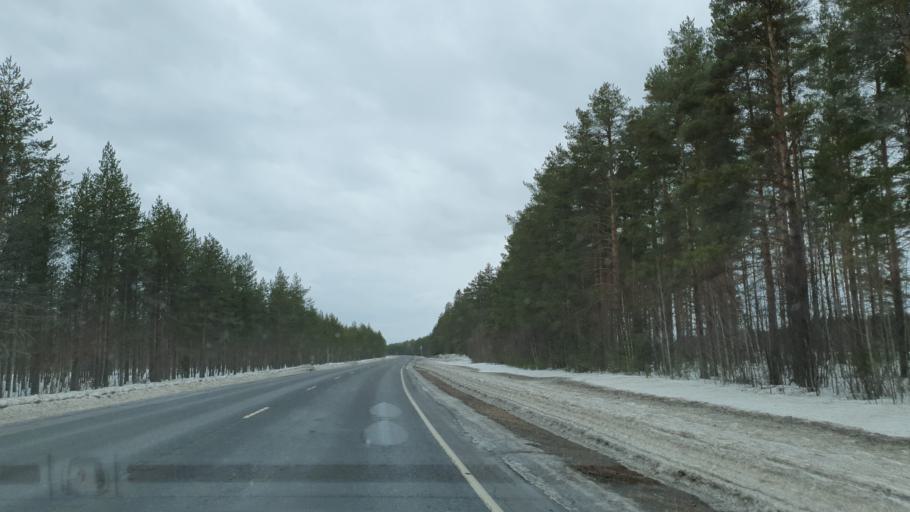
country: FI
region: Northern Ostrobothnia
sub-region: Oulunkaari
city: Utajaervi
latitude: 64.7277
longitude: 26.4875
